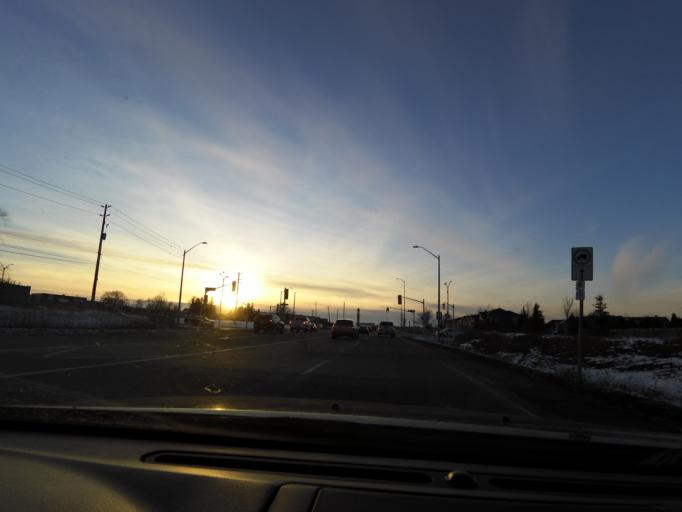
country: CA
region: Ontario
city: Hamilton
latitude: 43.1965
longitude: -79.8057
